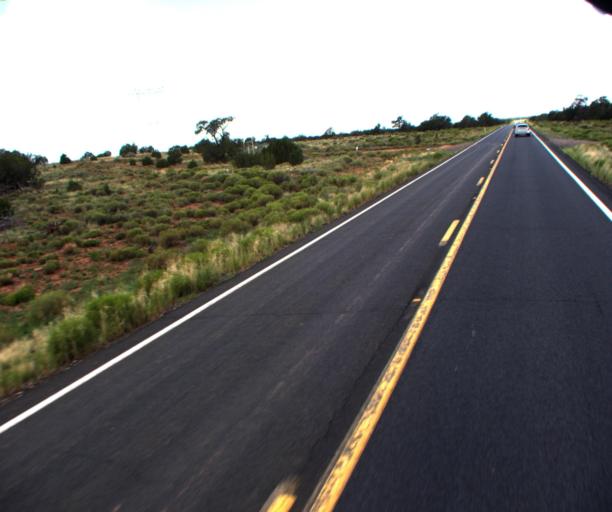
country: US
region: Arizona
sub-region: Coconino County
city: Parks
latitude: 35.5859
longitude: -111.9796
